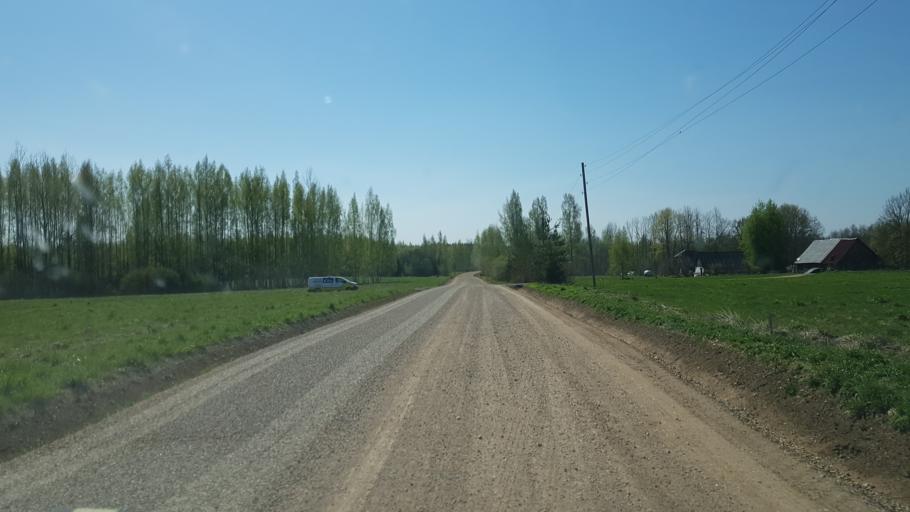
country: EE
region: Polvamaa
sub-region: Polva linn
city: Polva
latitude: 58.1169
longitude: 27.2382
